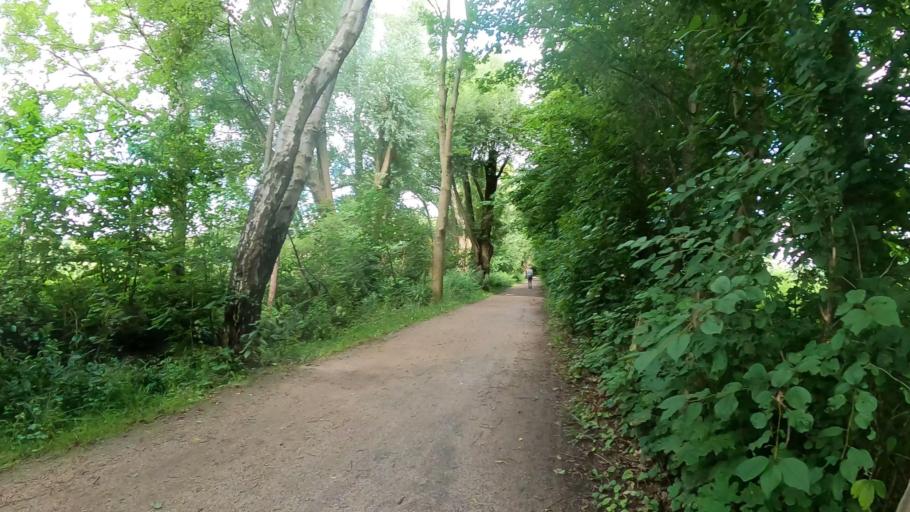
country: DE
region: Schleswig-Holstein
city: Bonningstedt
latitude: 53.6335
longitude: 9.9332
